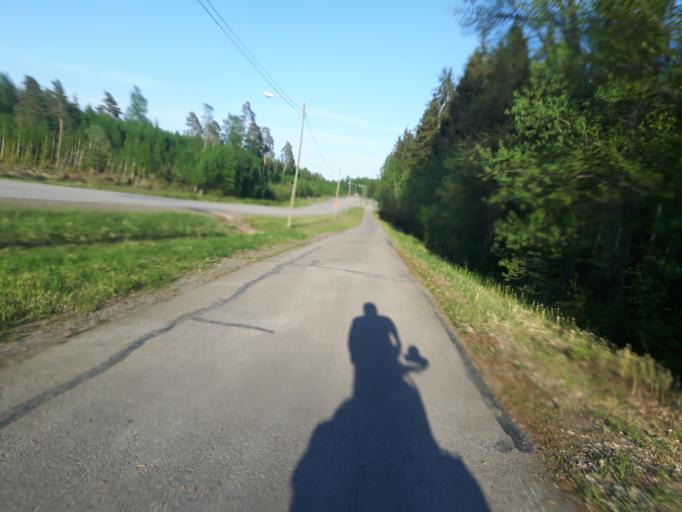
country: FI
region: Uusimaa
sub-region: Loviisa
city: Lovisa
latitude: 60.4554
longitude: 26.1581
